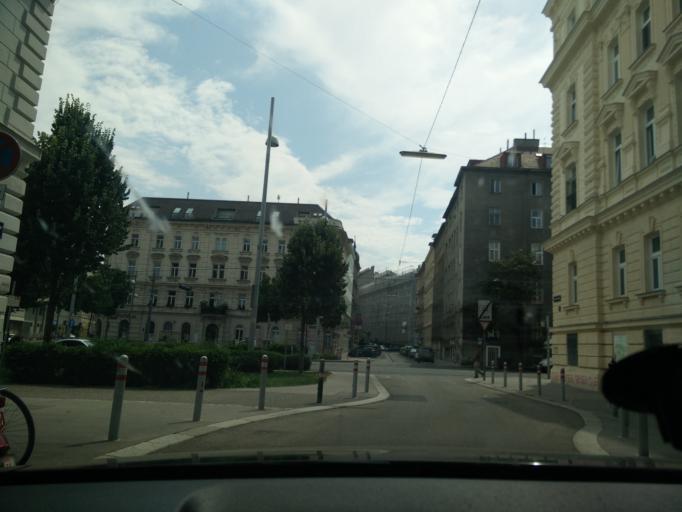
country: AT
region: Vienna
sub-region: Wien Stadt
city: Vienna
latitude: 48.2174
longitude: 16.3432
